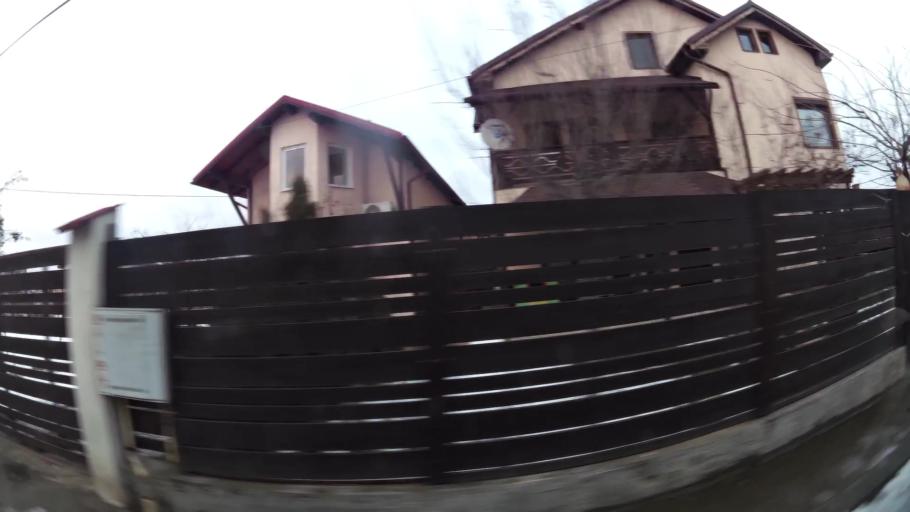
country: RO
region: Ilfov
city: Dobroesti
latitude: 44.4540
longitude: 26.1828
